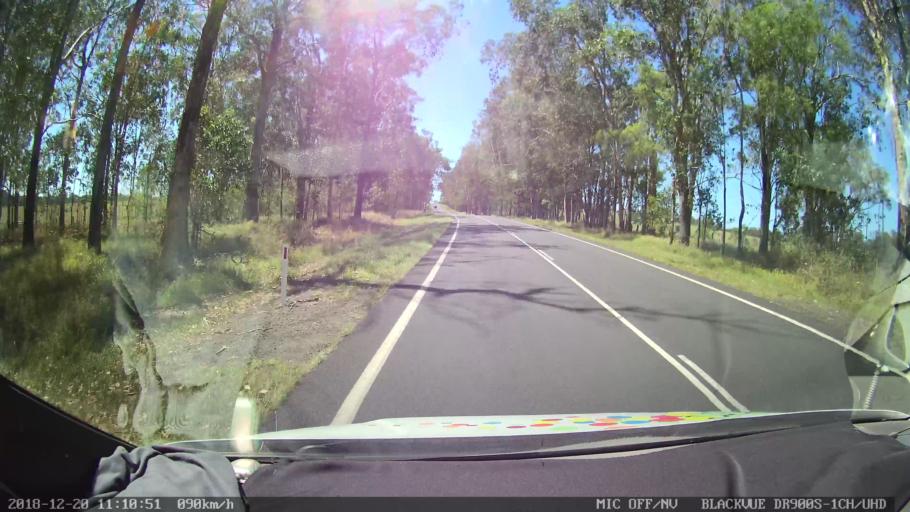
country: AU
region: New South Wales
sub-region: Richmond Valley
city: Casino
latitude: -28.9546
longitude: 153.0109
